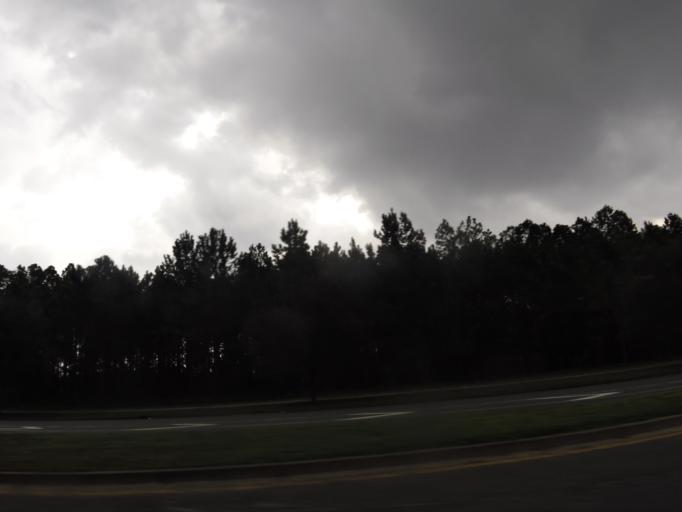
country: US
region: Florida
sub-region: Clay County
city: Lakeside
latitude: 30.1879
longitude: -81.8455
